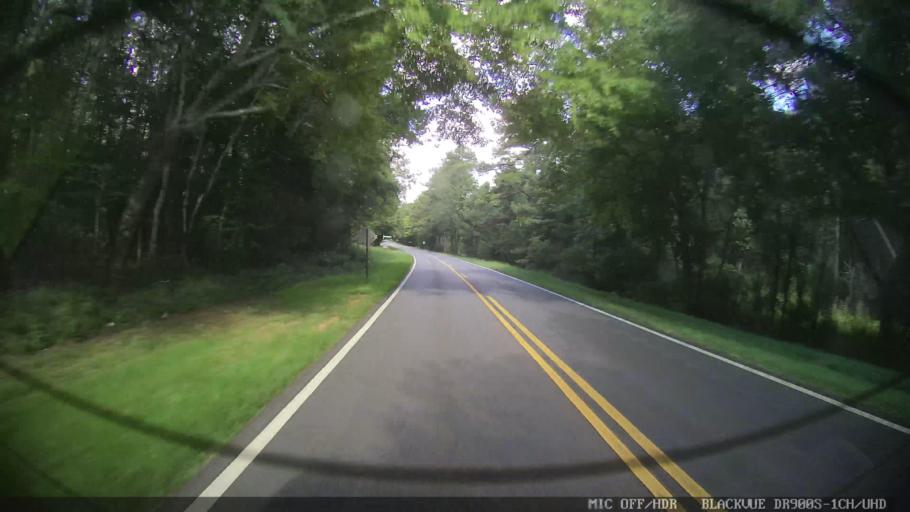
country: US
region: Georgia
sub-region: Bartow County
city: Euharlee
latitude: 34.1774
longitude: -85.0076
